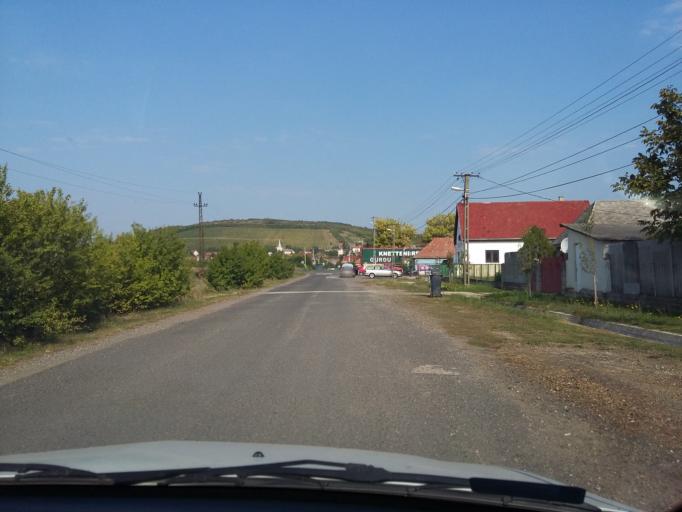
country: HU
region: Borsod-Abauj-Zemplen
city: Bekecs
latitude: 48.1464
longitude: 21.1803
